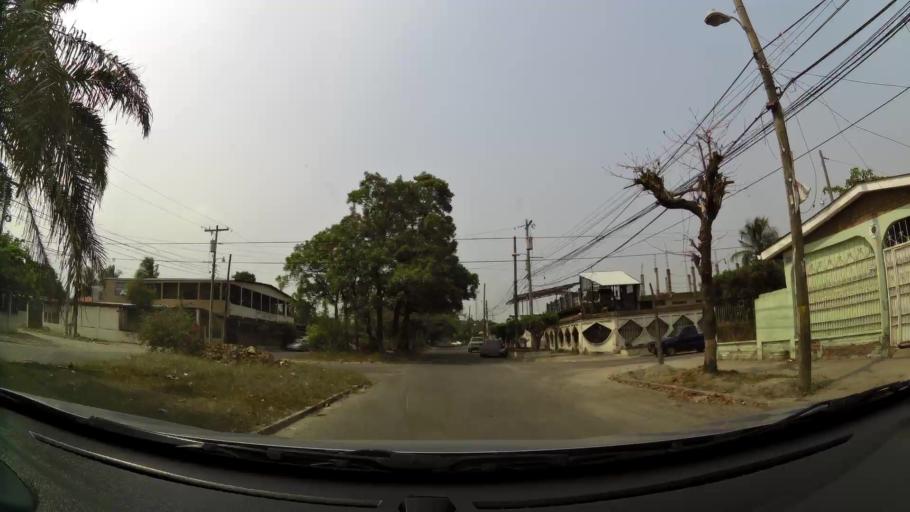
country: HN
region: Cortes
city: San Pedro Sula
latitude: 15.4828
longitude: -88.0173
